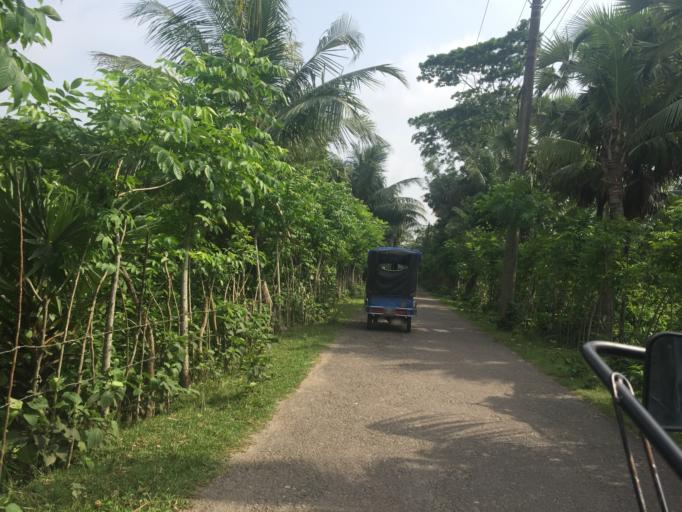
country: BD
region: Barisal
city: Mathba
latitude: 22.2200
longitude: 89.9160
